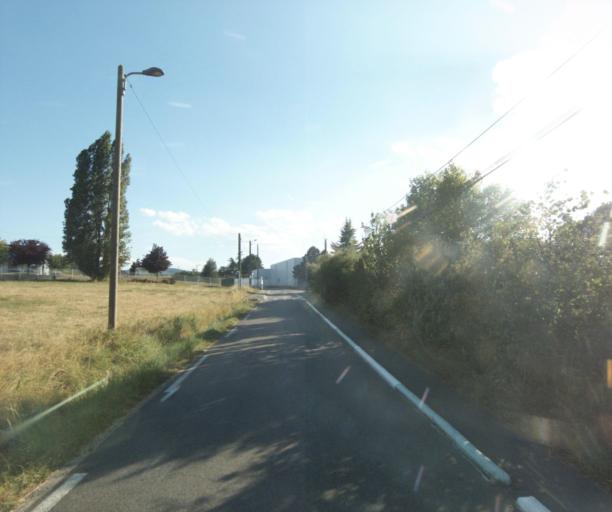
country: FR
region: Rhone-Alpes
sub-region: Departement du Rhone
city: Lentilly
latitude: 45.8268
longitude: 4.6725
